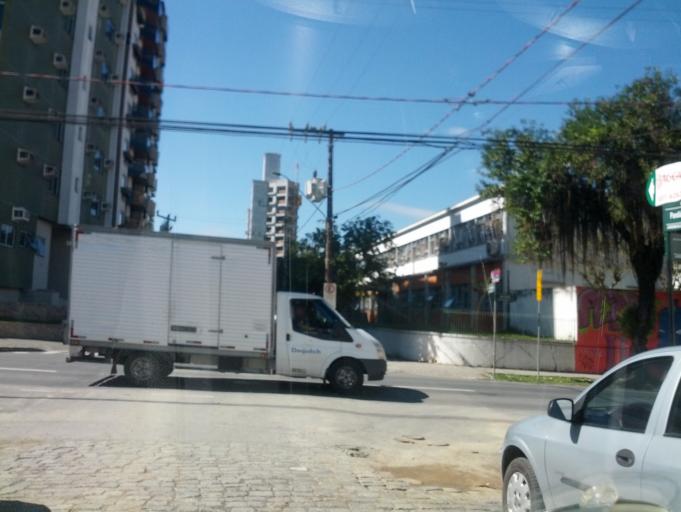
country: BR
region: Santa Catarina
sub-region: Blumenau
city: Blumenau
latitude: -26.9269
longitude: -49.0636
